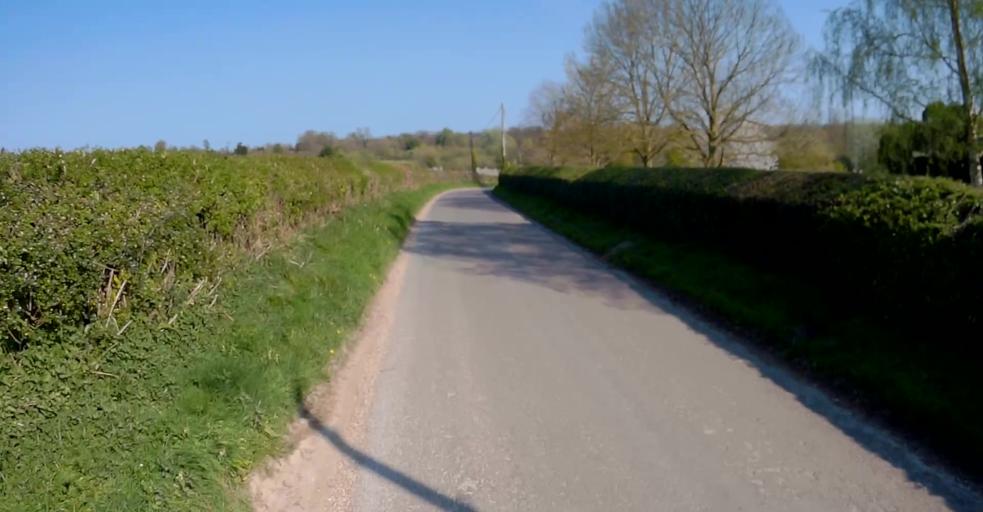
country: GB
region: England
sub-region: Hampshire
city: Four Marks
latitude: 51.0961
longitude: -1.1701
